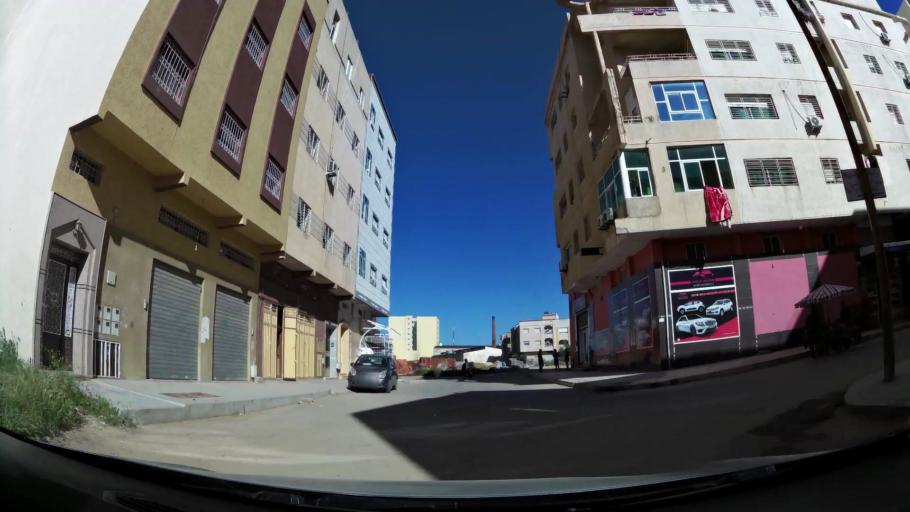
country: MA
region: Meknes-Tafilalet
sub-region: Meknes
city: Meknes
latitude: 33.8790
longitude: -5.5779
